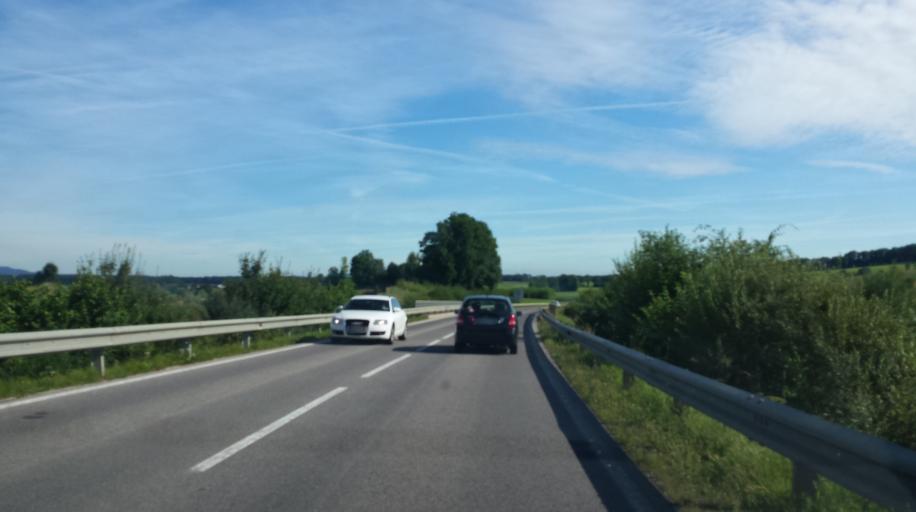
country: AT
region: Upper Austria
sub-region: Politischer Bezirk Vocklabruck
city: Sankt Georgen im Attergau
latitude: 47.9304
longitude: 13.5024
